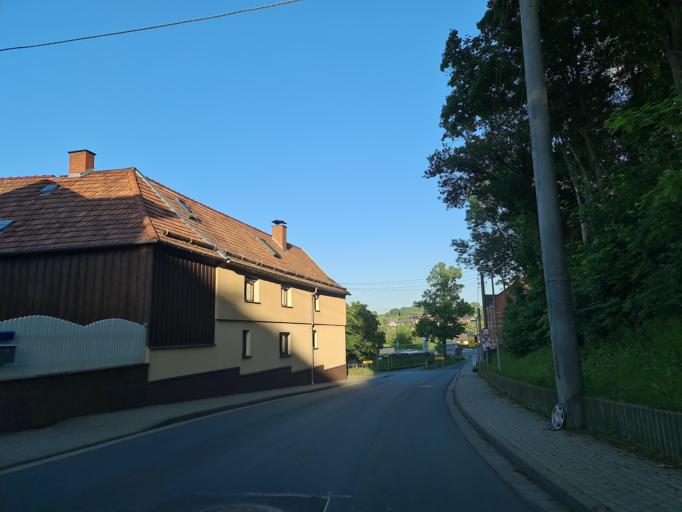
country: DE
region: Saxony
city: Weischlitz
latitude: 50.4480
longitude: 12.0571
